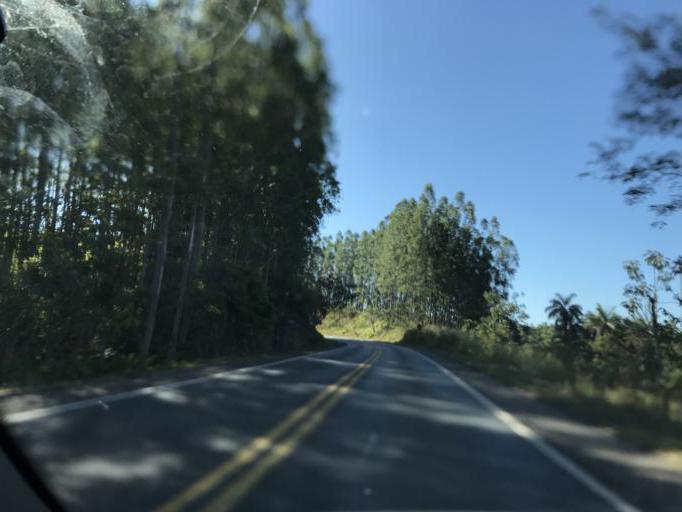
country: BR
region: Minas Gerais
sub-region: Bambui
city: Bambui
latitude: -19.8271
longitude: -46.0095
